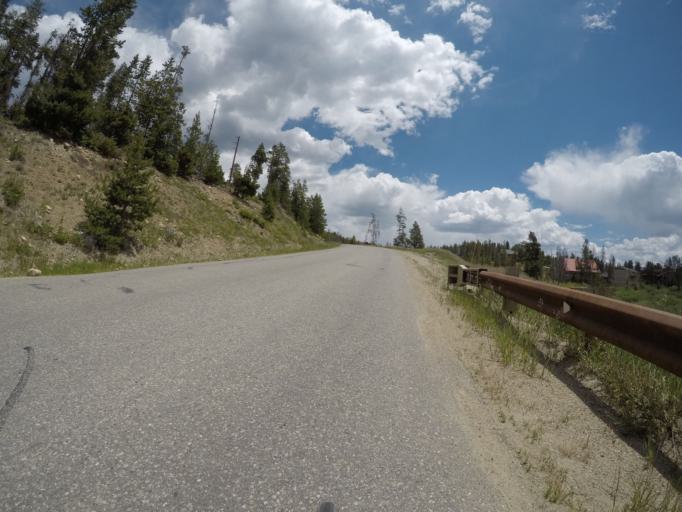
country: US
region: Colorado
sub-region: Grand County
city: Fraser
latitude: 39.9523
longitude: -105.8083
